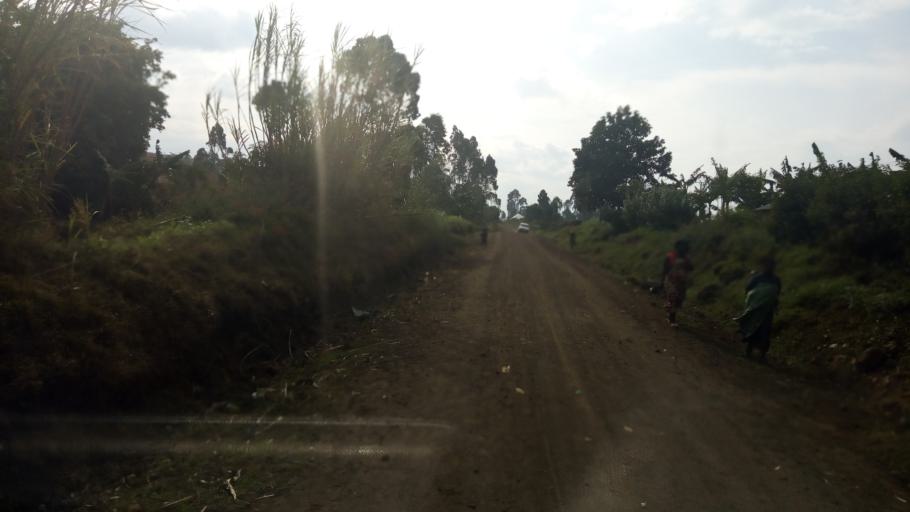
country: UG
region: Western Region
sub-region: Kisoro District
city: Kisoro
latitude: -1.3123
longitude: 29.7201
